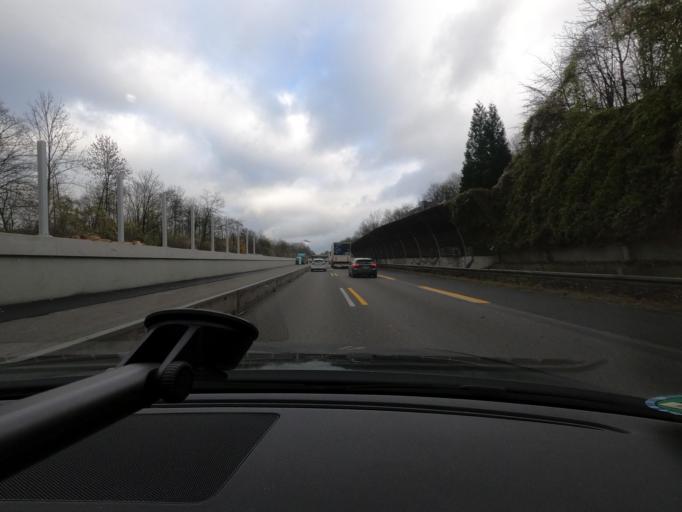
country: DE
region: North Rhine-Westphalia
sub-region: Regierungsbezirk Dusseldorf
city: Essen
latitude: 51.4297
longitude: 7.0180
